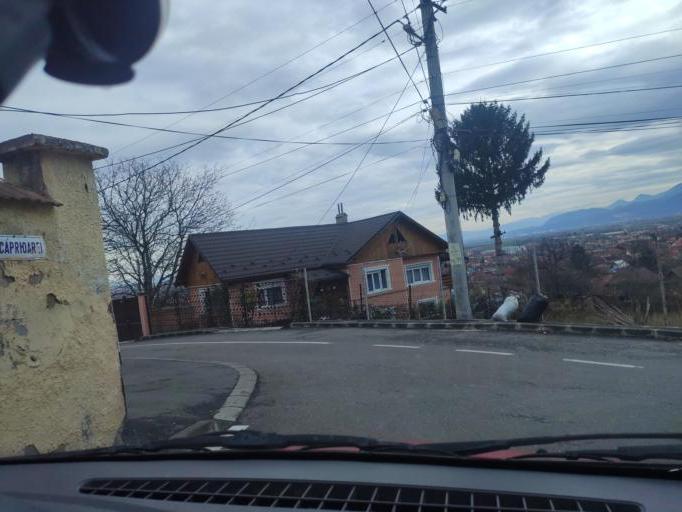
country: RO
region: Brasov
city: Codlea
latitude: 45.6984
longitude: 25.4355
